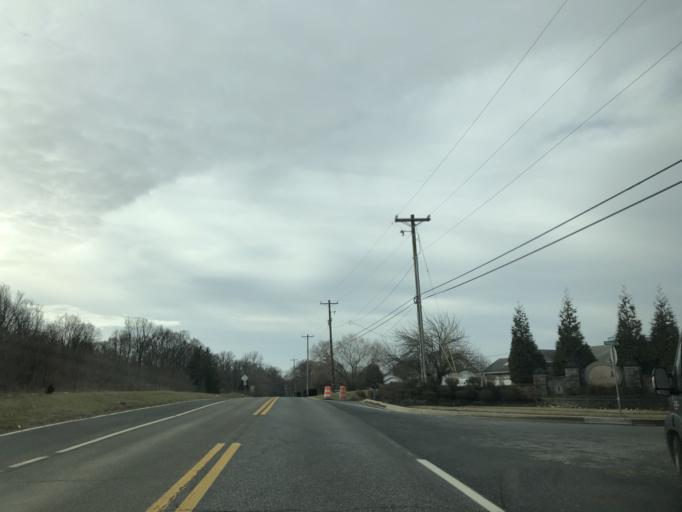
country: US
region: Delaware
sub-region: New Castle County
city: Middletown
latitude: 39.4890
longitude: -75.6938
